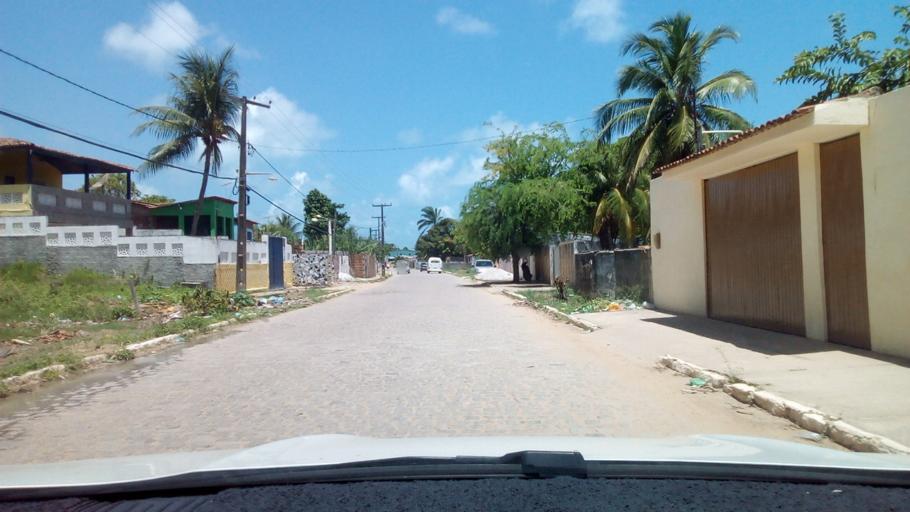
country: BR
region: Paraiba
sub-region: Pitimbu
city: Pitimbu
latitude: -7.4809
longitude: -34.8135
